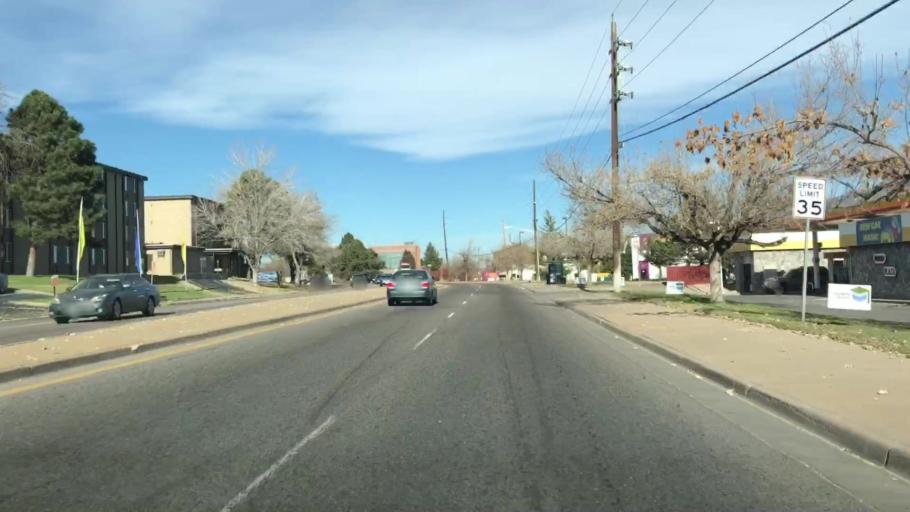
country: US
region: Colorado
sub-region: Arapahoe County
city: Glendale
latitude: 39.6772
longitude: -104.9041
